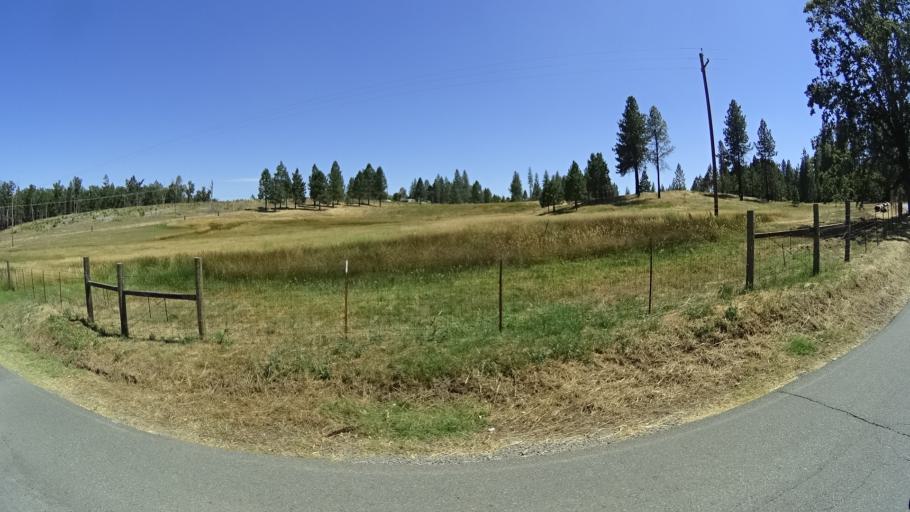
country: US
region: California
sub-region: Calaveras County
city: Mountain Ranch
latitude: 38.2844
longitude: -120.5183
